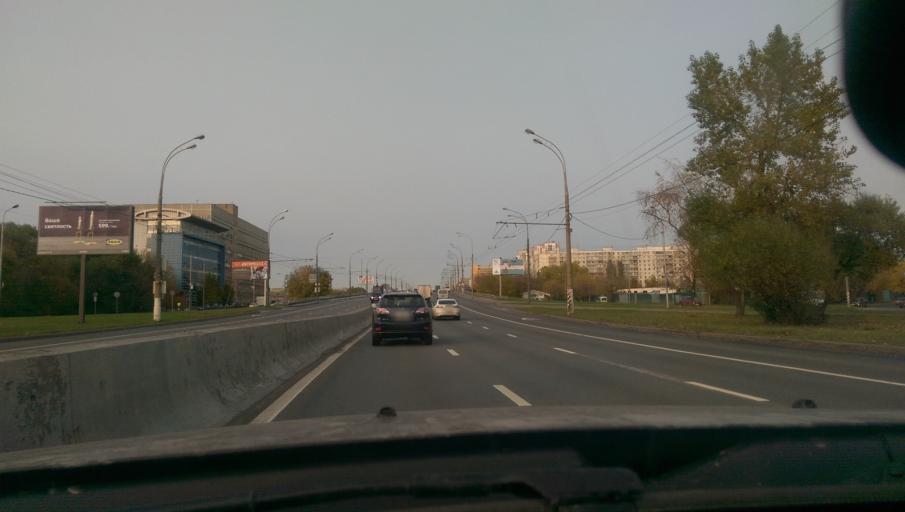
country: RU
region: Moscow
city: Slobodka
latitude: 55.8667
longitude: 37.5844
